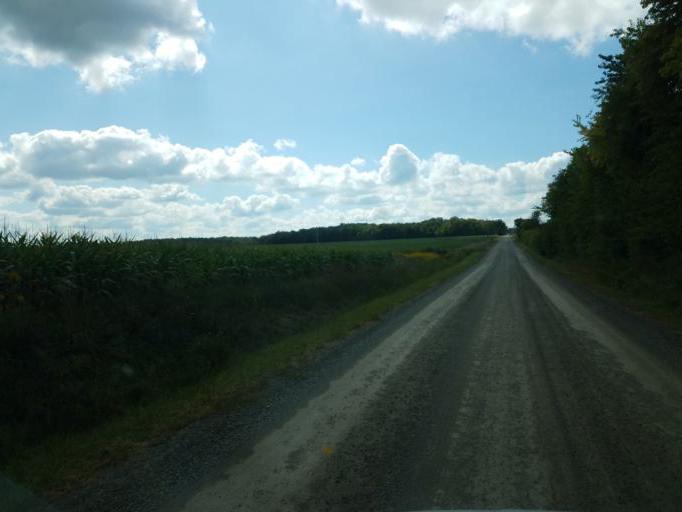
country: US
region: Ohio
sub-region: Medina County
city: Lodi
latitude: 41.0585
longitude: -82.0960
